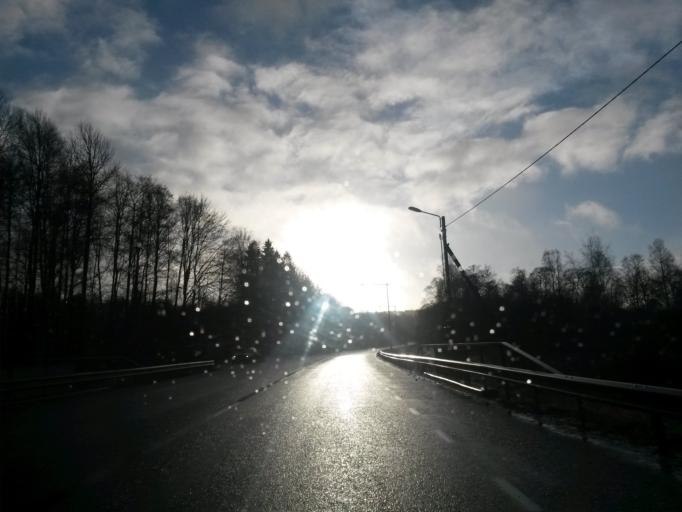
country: SE
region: Vaestra Goetaland
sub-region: Boras Kommun
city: Ganghester
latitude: 57.7984
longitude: 13.0110
